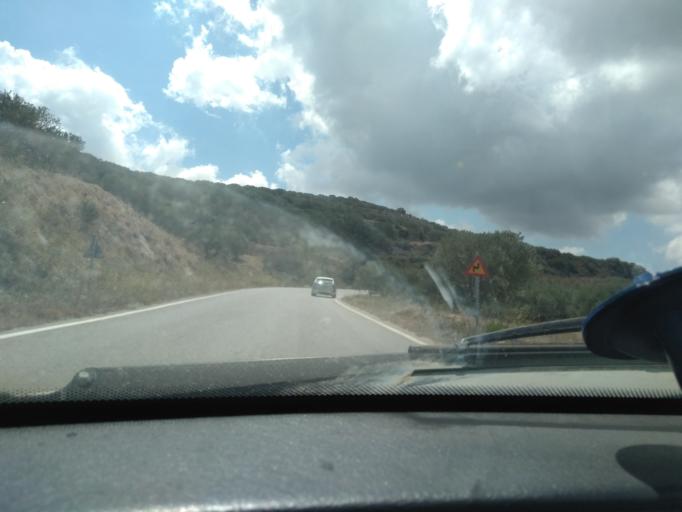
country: GR
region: Crete
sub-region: Nomos Lasithiou
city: Siteia
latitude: 35.0992
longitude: 26.0720
